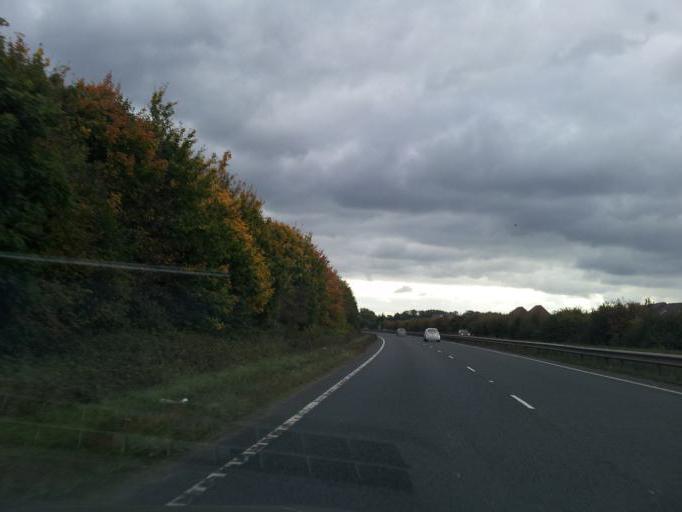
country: GB
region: England
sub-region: Northamptonshire
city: Blisworth
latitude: 52.2171
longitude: -0.9376
